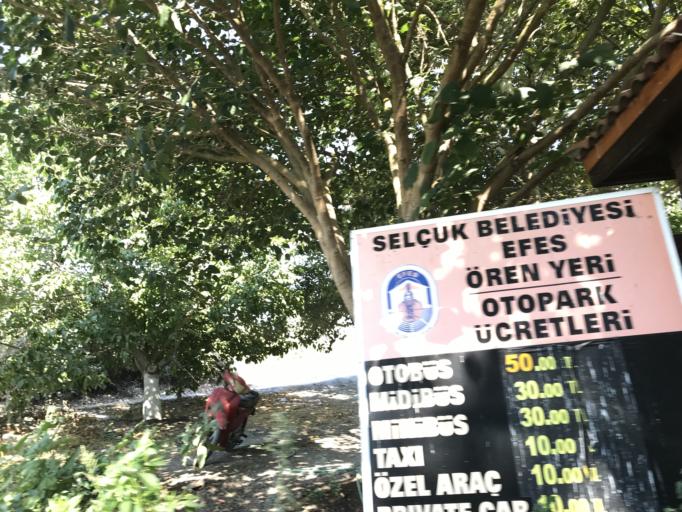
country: TR
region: Izmir
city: Selcuk
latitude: 37.9459
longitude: 27.3421
